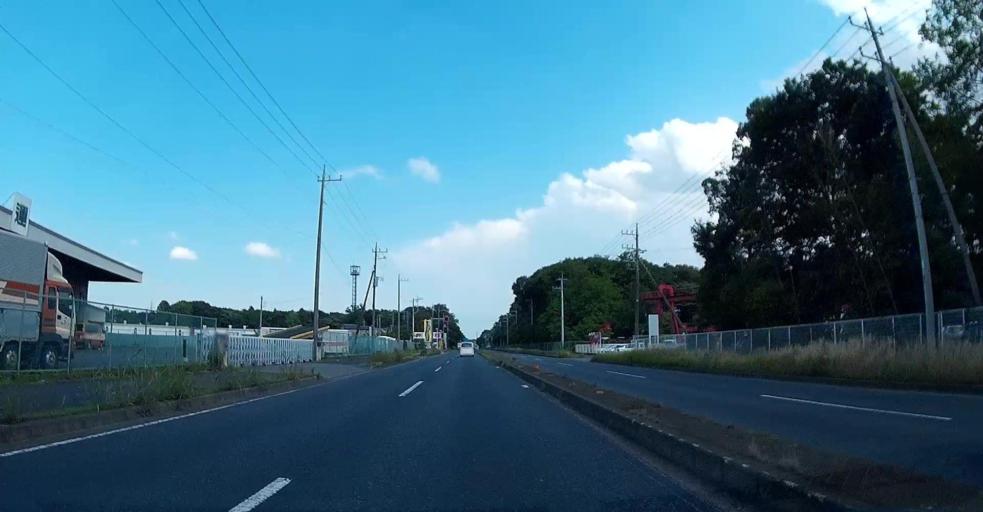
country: JP
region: Chiba
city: Noda
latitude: 35.9890
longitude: 139.8533
